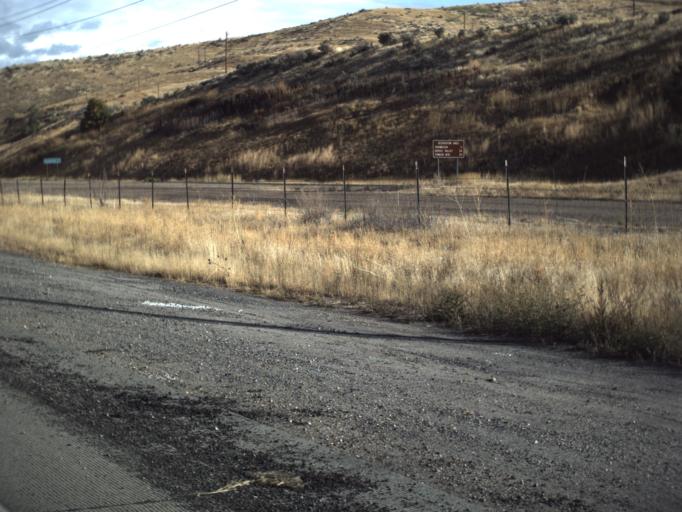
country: US
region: Utah
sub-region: Morgan County
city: Mountain Green
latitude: 41.1167
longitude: -111.7635
